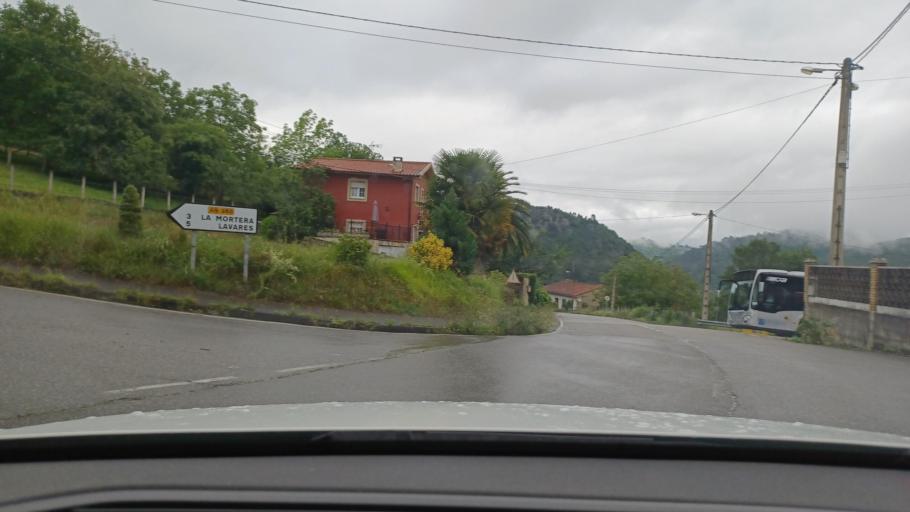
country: ES
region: Asturias
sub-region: Province of Asturias
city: Castandiello
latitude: 43.3162
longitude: -5.9253
